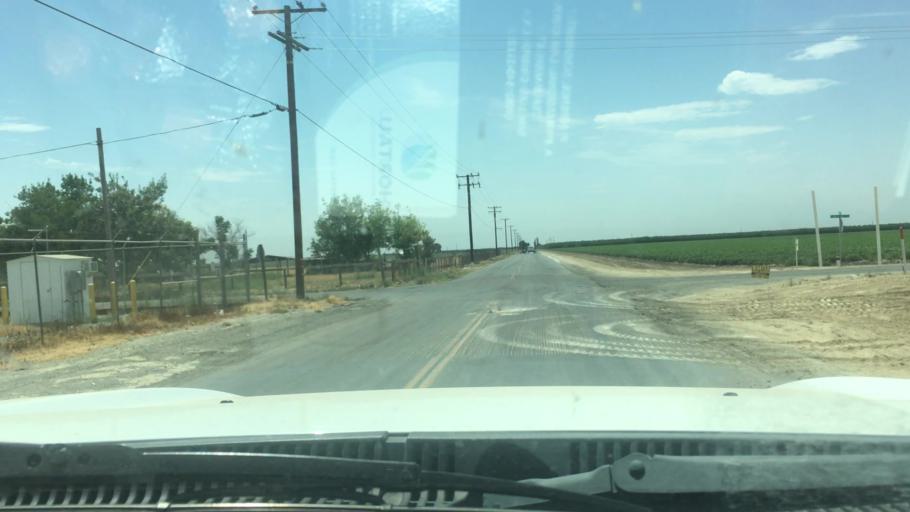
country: US
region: California
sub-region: Tulare County
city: Tipton
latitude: 36.0658
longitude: -119.3215
